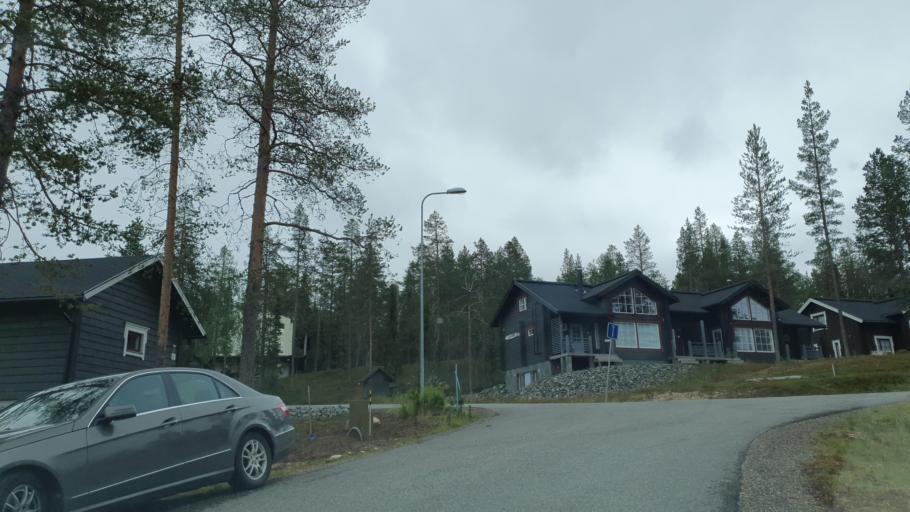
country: FI
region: Lapland
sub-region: Tunturi-Lappi
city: Kolari
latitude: 67.5934
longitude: 24.1782
